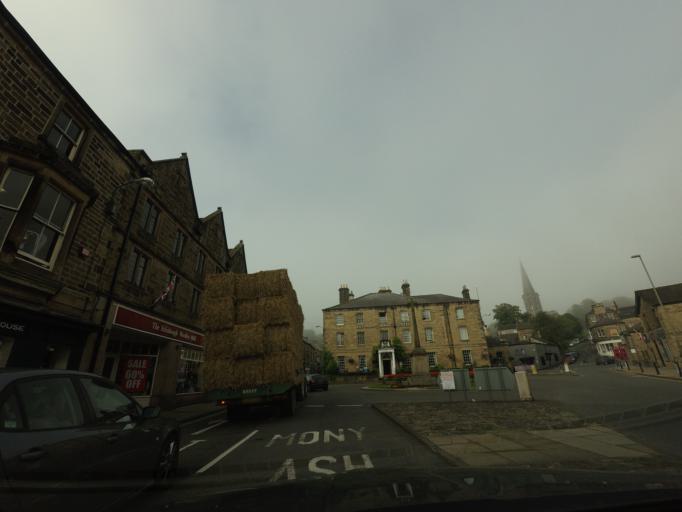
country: GB
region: England
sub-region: Derbyshire
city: Bakewell
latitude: 53.2131
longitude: -1.6754
